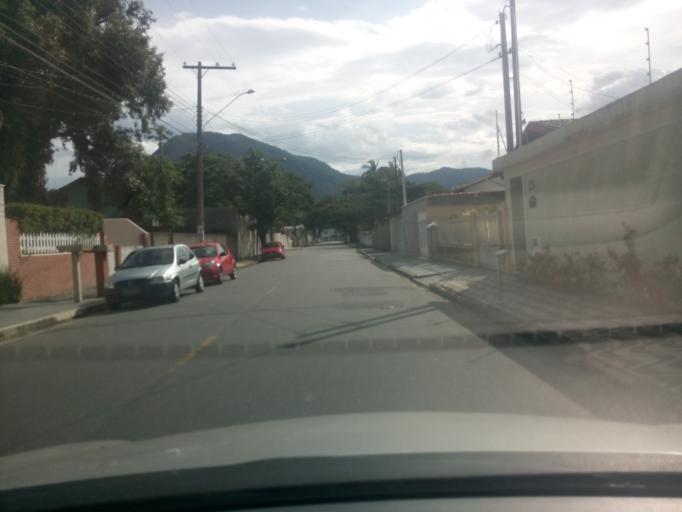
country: BR
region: Sao Paulo
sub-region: Peruibe
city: Peruibe
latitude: -24.3196
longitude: -47.0004
